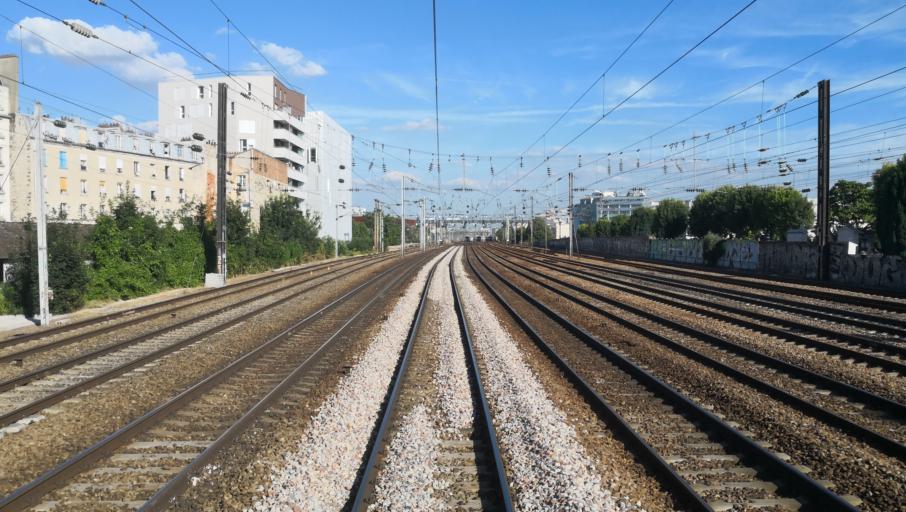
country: FR
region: Ile-de-France
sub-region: Departement des Hauts-de-Seine
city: Levallois-Perret
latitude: 48.9027
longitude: 2.2891
